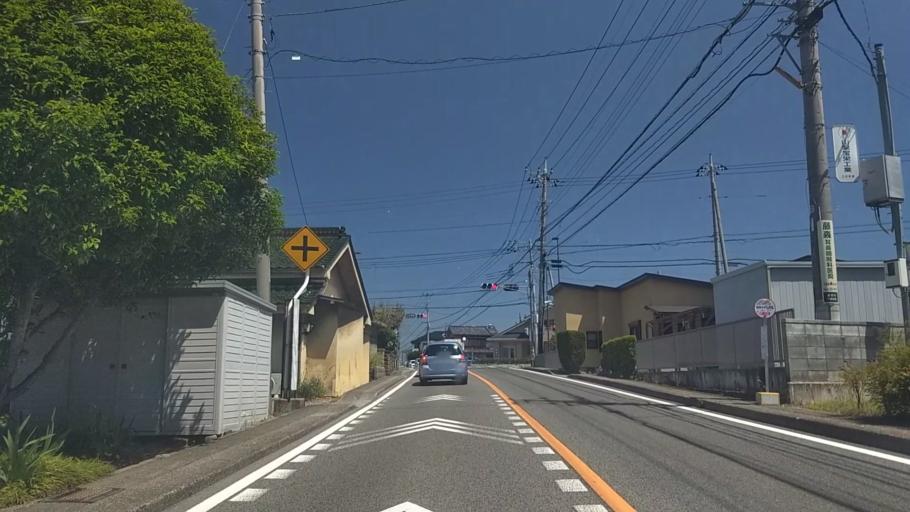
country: JP
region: Yamanashi
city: Nirasaki
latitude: 35.6778
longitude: 138.4649
